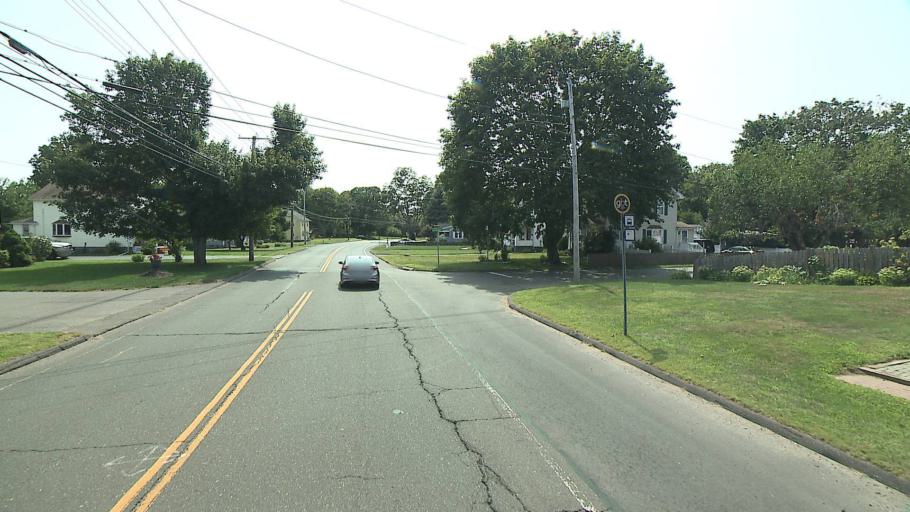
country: US
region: Connecticut
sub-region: Fairfield County
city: Stratford
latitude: 41.2217
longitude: -73.1175
